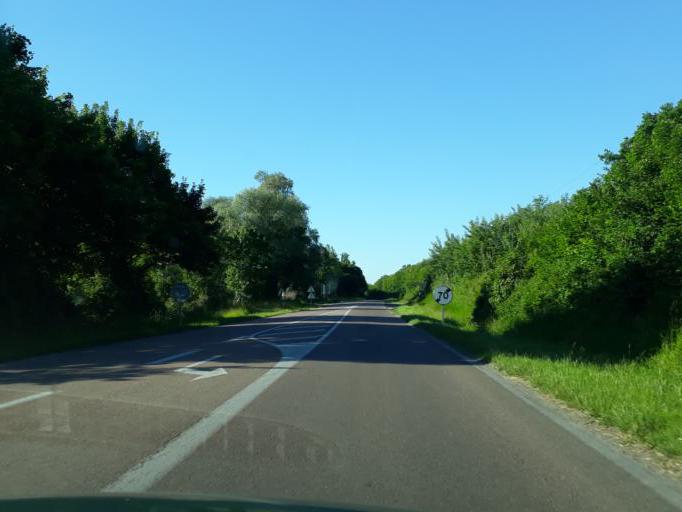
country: FR
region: Bourgogne
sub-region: Departement de la Nievre
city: Cosne-Cours-sur-Loire
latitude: 47.4276
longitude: 2.9322
